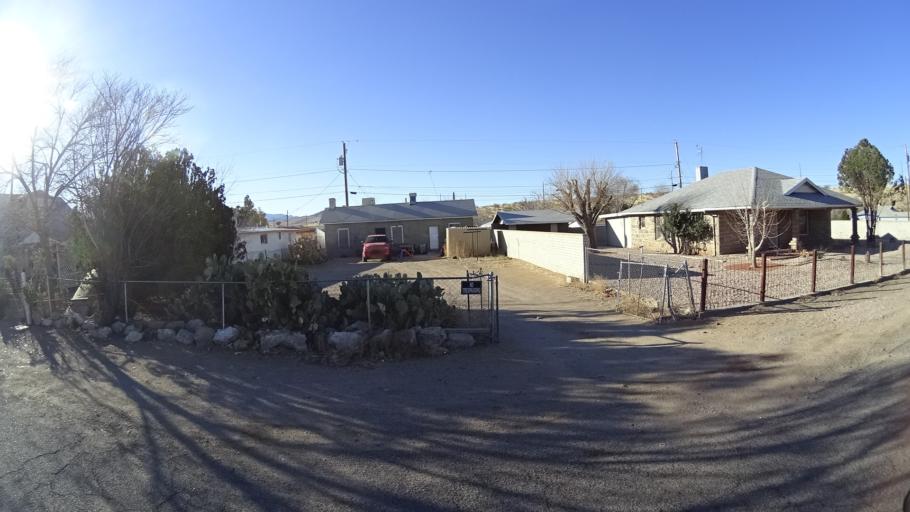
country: US
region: Arizona
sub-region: Mohave County
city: Kingman
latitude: 35.1847
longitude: -114.0439
